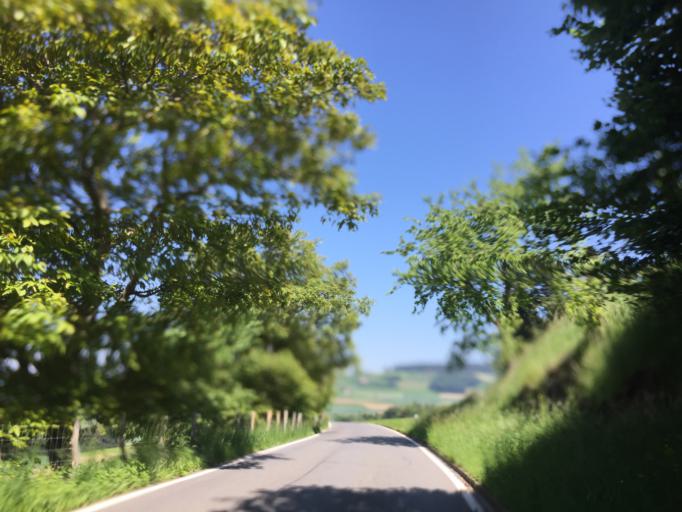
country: CH
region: Bern
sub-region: Bern-Mittelland District
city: Taegertschi
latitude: 46.8622
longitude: 7.6015
